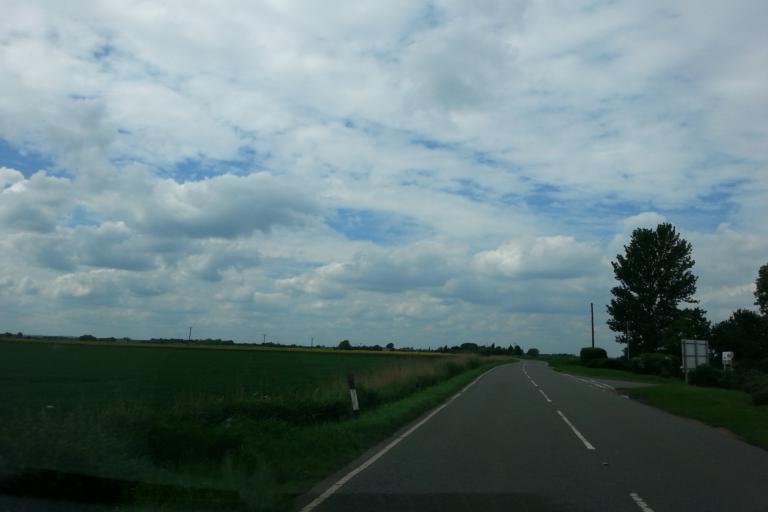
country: GB
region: England
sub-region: Cambridgeshire
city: Ramsey
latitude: 52.4608
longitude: -0.1216
